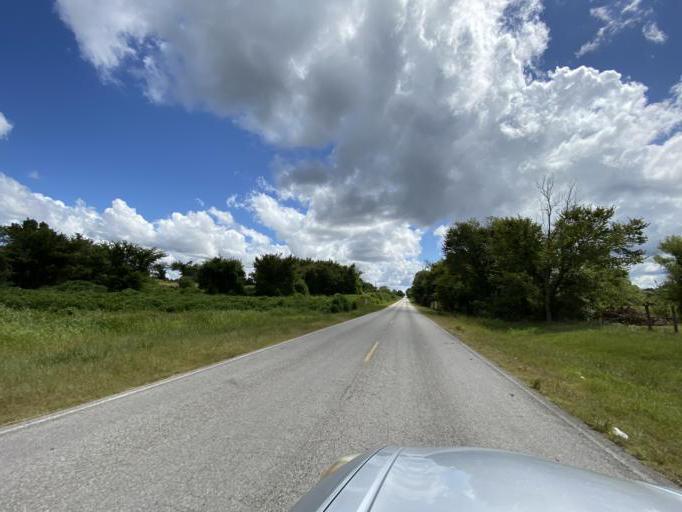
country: US
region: Mississippi
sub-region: Panola County
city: Como
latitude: 34.5104
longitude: -89.9980
